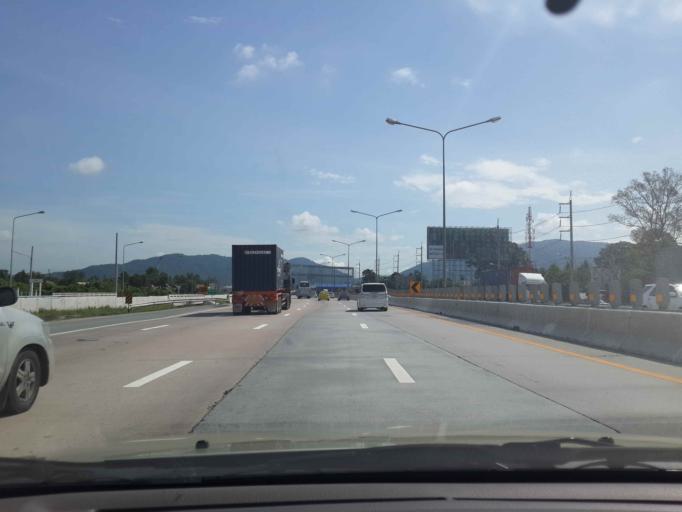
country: TH
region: Chon Buri
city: Si Racha
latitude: 13.2093
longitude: 101.0046
